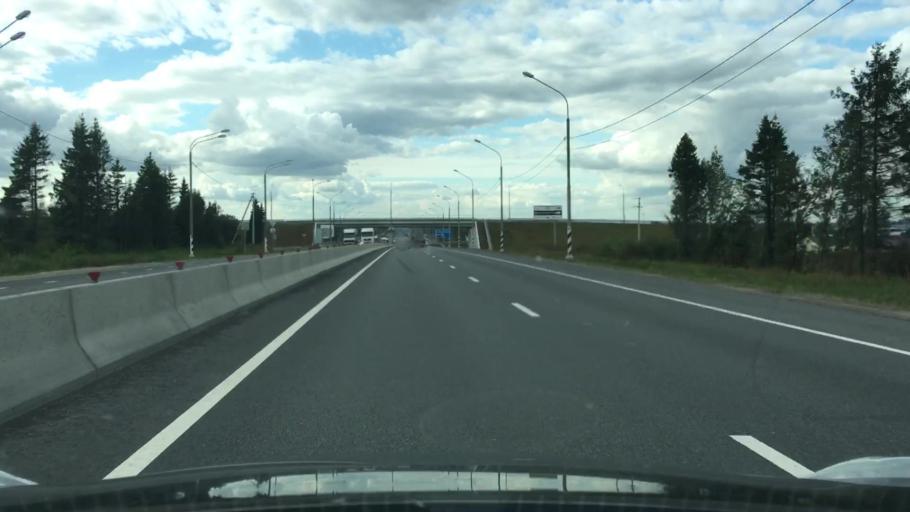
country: RU
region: Tverskaya
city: Tver
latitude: 56.7863
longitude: 35.9261
